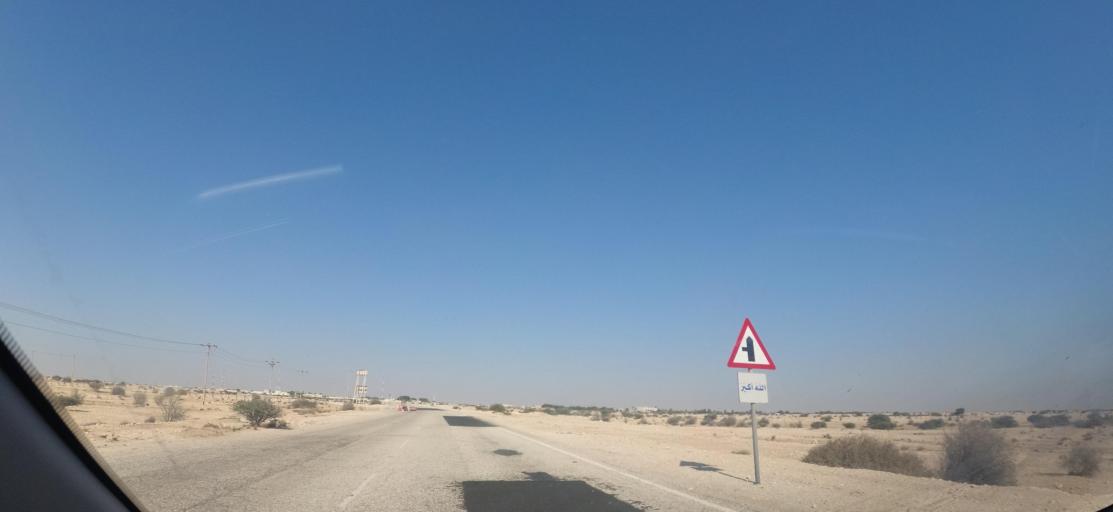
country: QA
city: Al Jumayliyah
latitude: 25.6056
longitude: 51.0757
